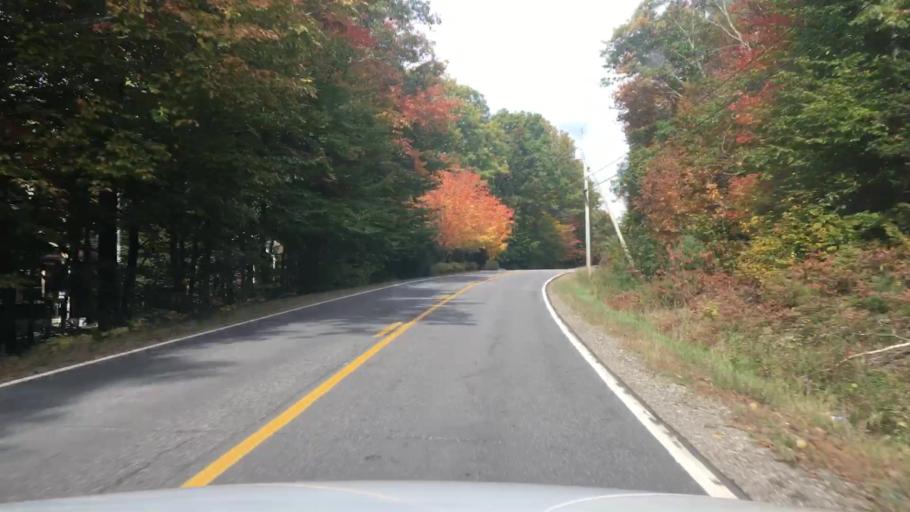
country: US
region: Maine
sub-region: Knox County
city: Hope
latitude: 44.3187
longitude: -69.1253
